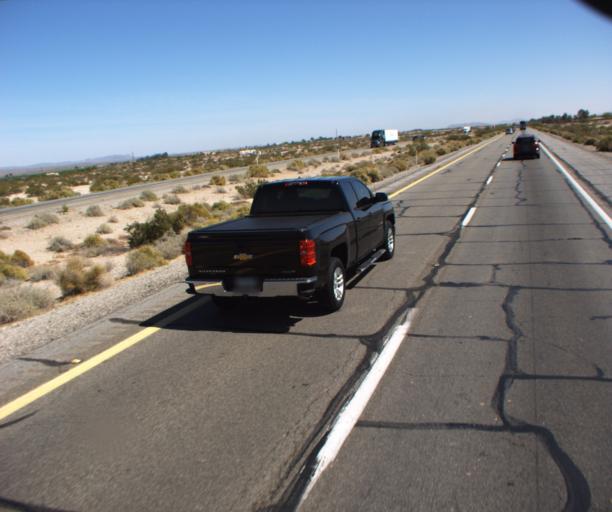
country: US
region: Arizona
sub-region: Yuma County
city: Wellton
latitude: 32.6501
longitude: -114.1913
